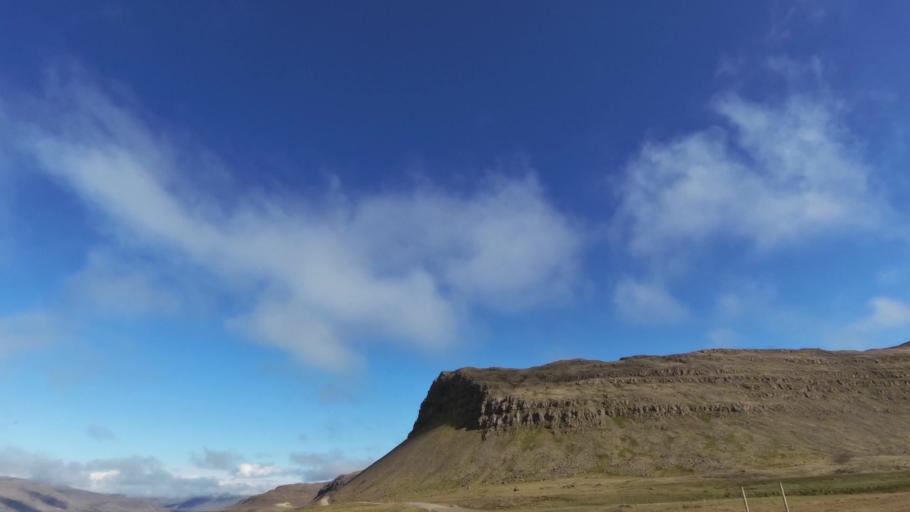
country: IS
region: West
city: Olafsvik
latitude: 65.5708
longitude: -24.0607
